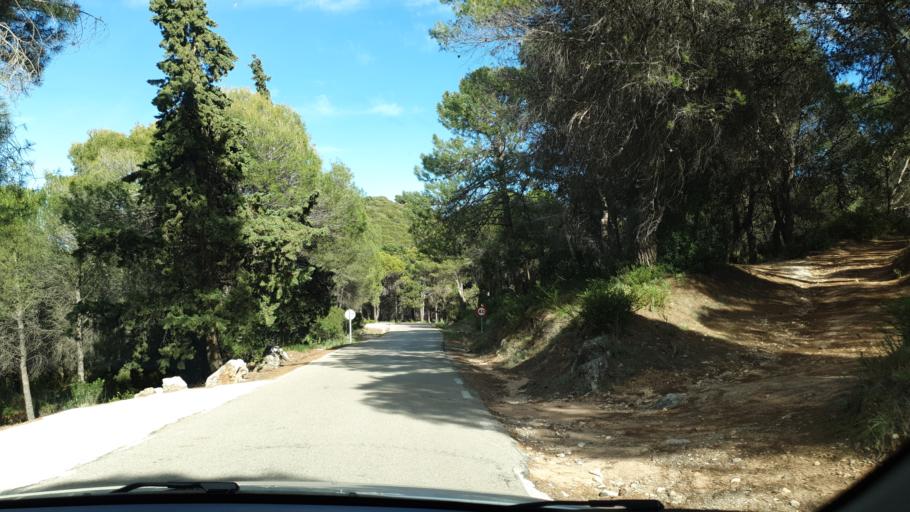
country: ES
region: Andalusia
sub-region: Provincia de Malaga
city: Ojen
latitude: 36.5876
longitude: -4.8612
